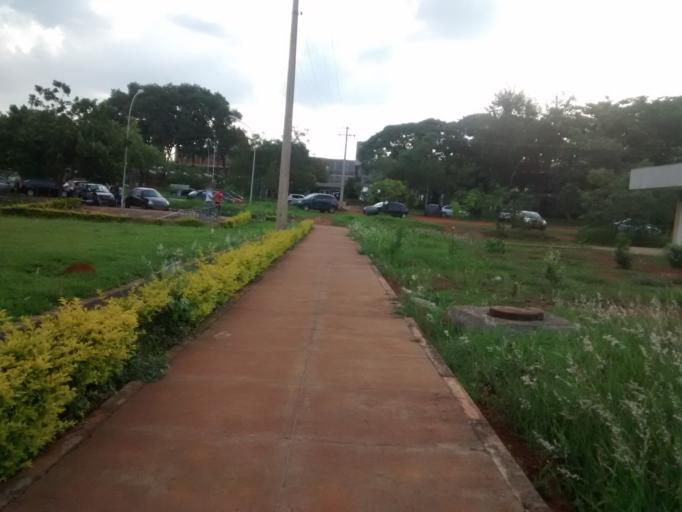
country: BR
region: Federal District
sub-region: Brasilia
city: Brasilia
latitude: -15.7680
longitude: -47.8653
